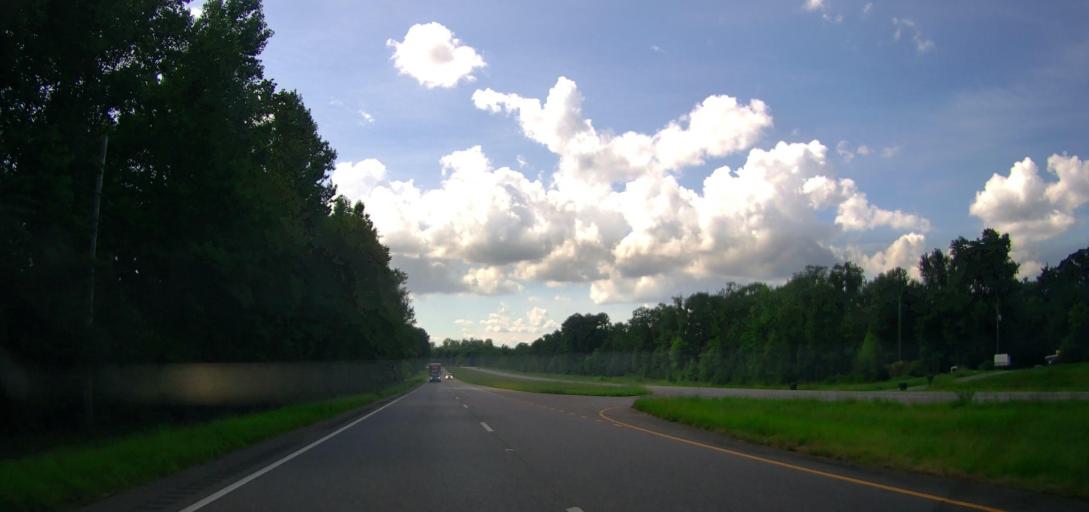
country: US
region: Alabama
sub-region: Pickens County
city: Reform
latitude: 33.3665
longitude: -87.9827
